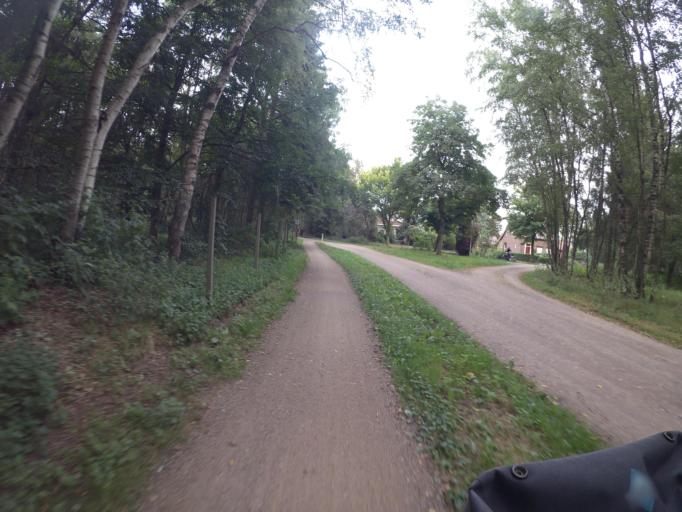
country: NL
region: Limburg
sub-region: Gemeente Gennep
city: Gennep
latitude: 51.6421
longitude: 6.0546
